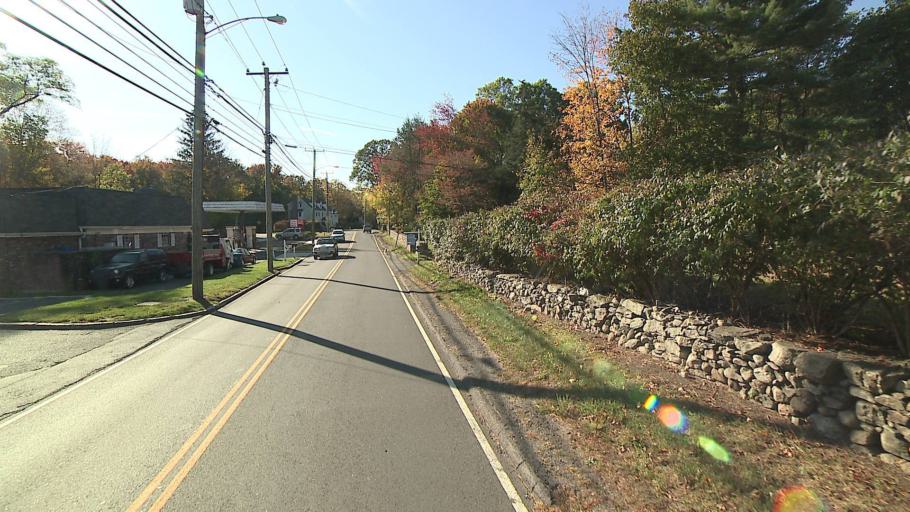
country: US
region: Connecticut
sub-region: Fairfield County
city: Norwalk
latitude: 41.1464
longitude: -73.3949
